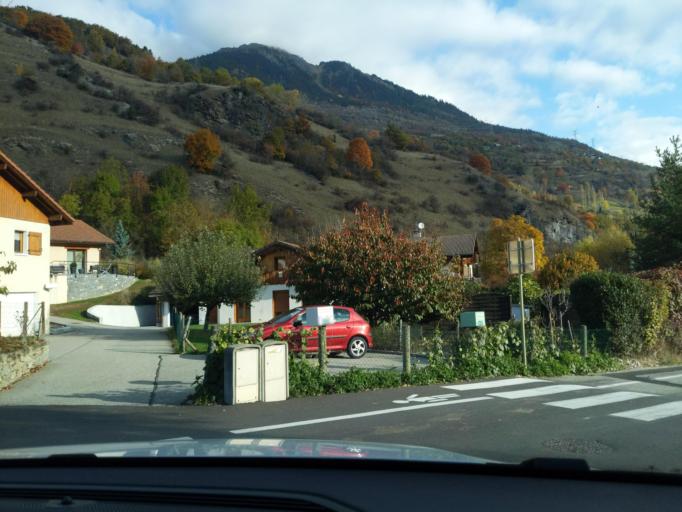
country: FR
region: Rhone-Alpes
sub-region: Departement de la Savoie
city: Aime
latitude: 45.5488
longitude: 6.6143
